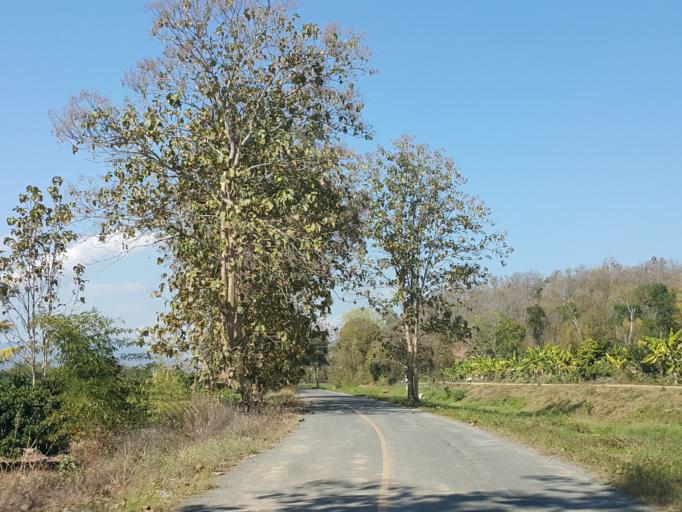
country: TH
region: Chiang Mai
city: Mae Taeng
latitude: 19.0765
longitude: 98.9562
